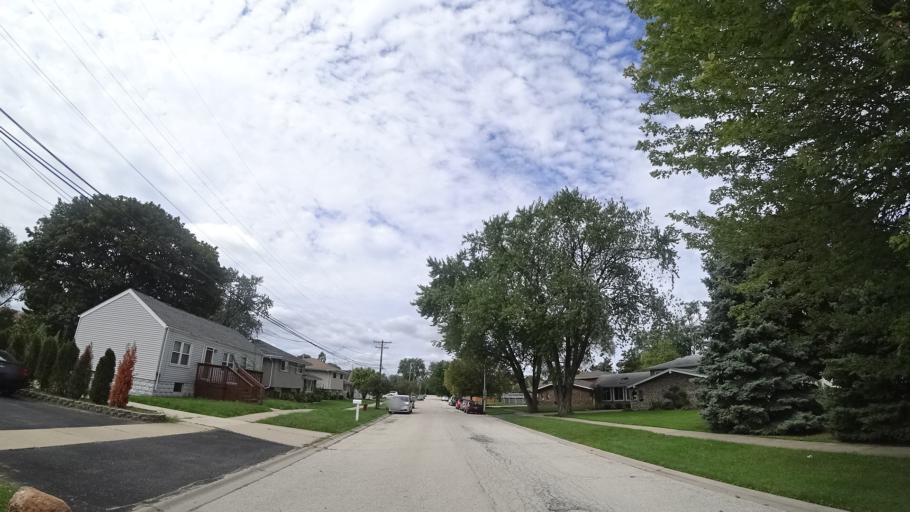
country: US
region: Illinois
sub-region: Cook County
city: Chicago Ridge
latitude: 41.7155
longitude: -87.7943
